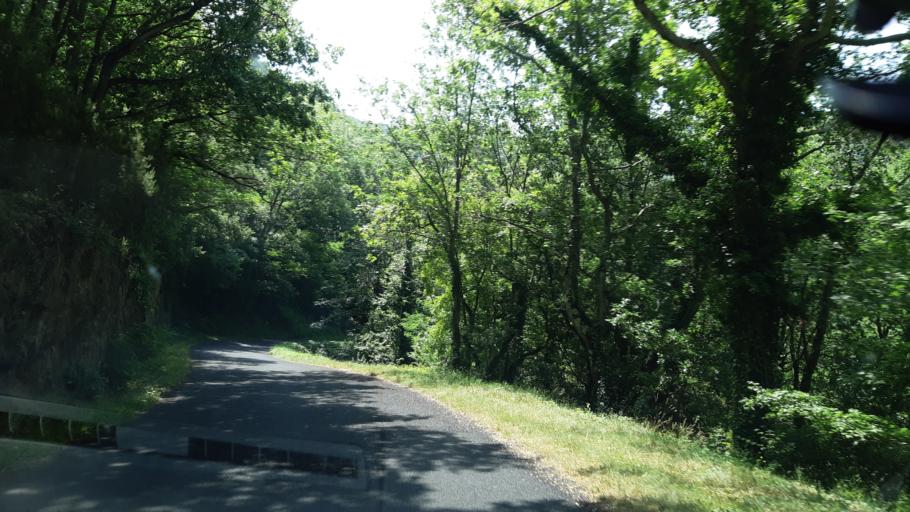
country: FR
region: Languedoc-Roussillon
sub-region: Departement des Pyrenees-Orientales
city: Arles
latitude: 42.5239
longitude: 2.6185
